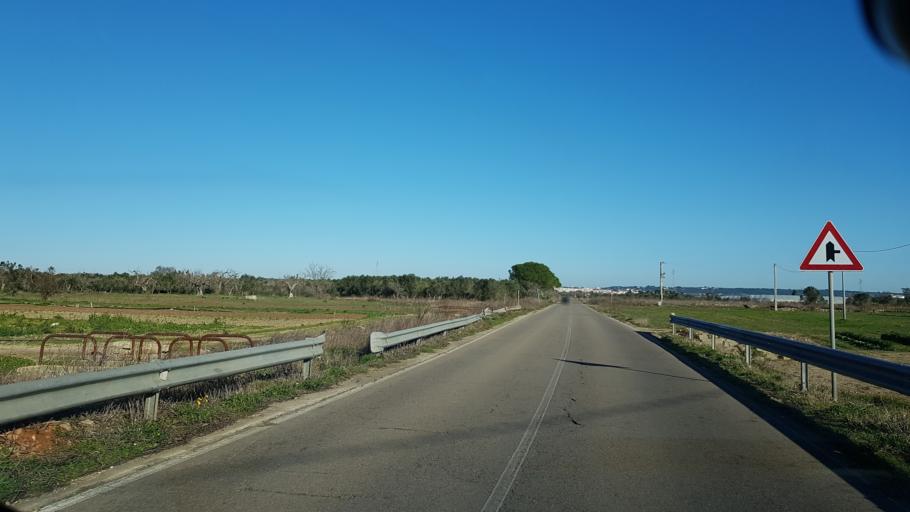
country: IT
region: Apulia
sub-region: Provincia di Lecce
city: Melissano
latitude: 39.9917
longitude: 18.1063
